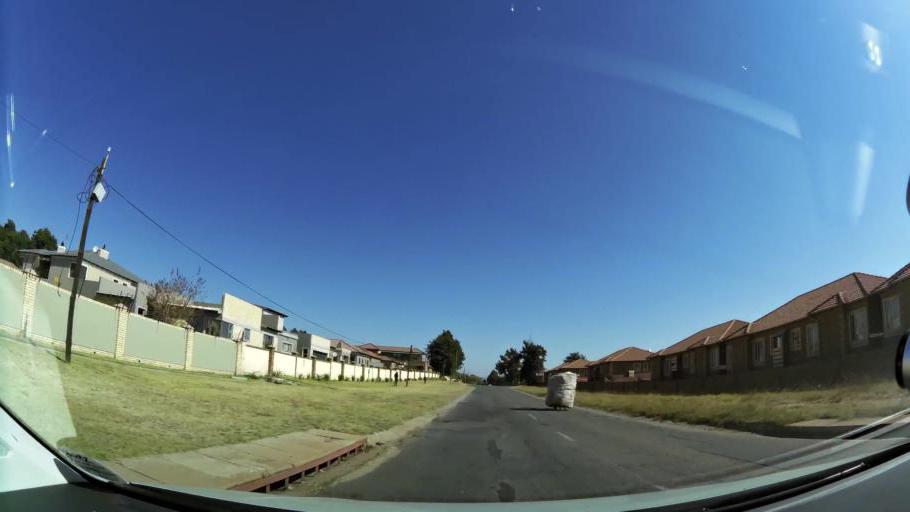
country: ZA
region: Gauteng
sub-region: City of Johannesburg Metropolitan Municipality
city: Modderfontein
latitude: -26.0709
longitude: 28.2022
